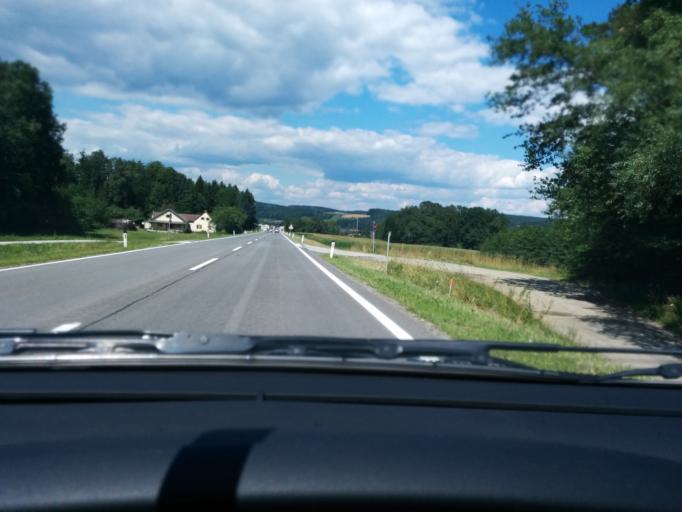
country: AT
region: Styria
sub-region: Politischer Bezirk Hartberg-Fuerstenfeld
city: Grafendorf bei Hartberg
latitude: 47.3189
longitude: 15.9852
